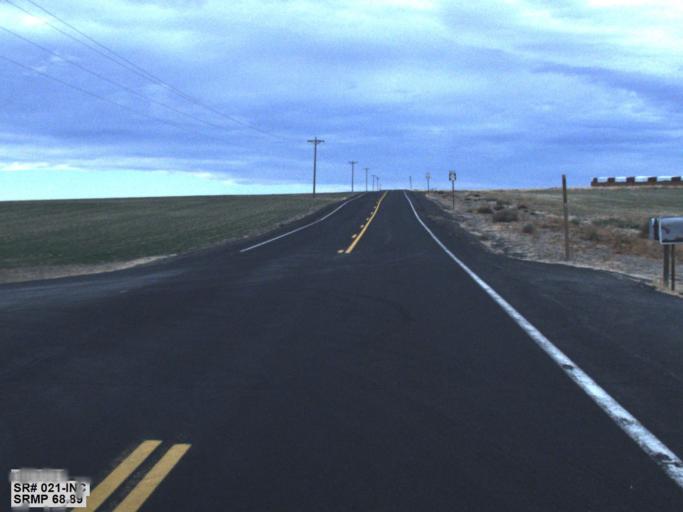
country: US
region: Washington
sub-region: Okanogan County
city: Coulee Dam
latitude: 47.4796
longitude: -118.7849
